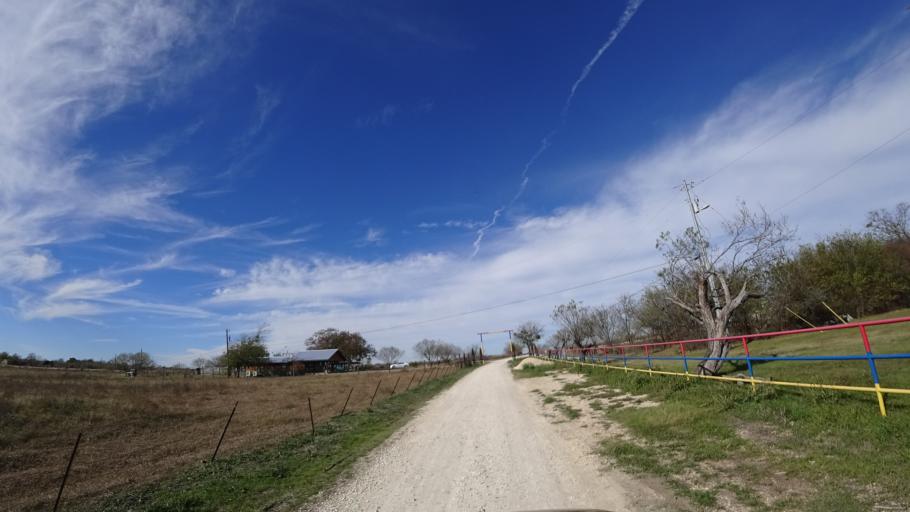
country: US
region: Texas
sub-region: Travis County
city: Onion Creek
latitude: 30.1157
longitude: -97.6824
